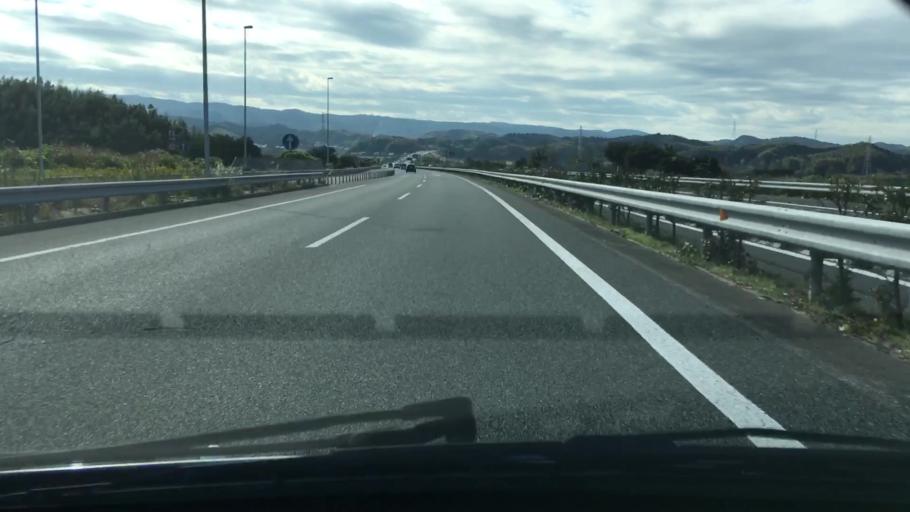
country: JP
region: Chiba
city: Kimitsu
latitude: 35.3197
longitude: 139.9441
